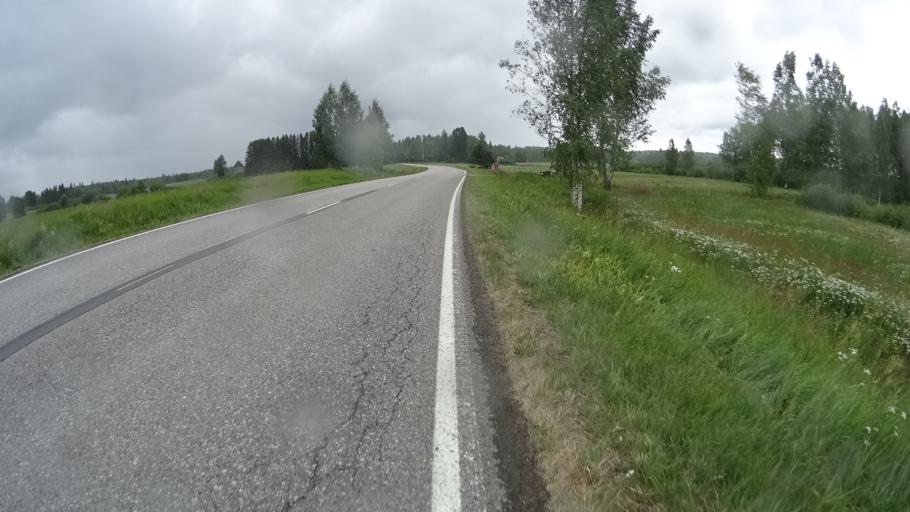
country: FI
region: Uusimaa
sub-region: Helsinki
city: Karkkila
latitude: 60.5817
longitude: 24.3378
